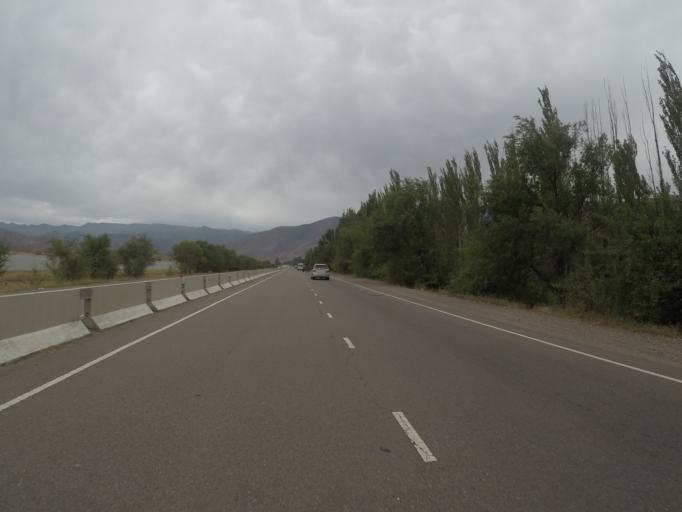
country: KG
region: Chuy
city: Bystrovka
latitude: 42.7452
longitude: 75.8328
